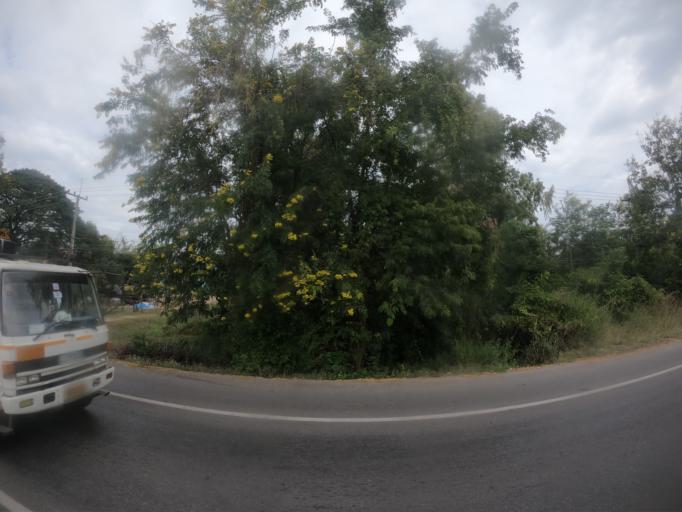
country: TH
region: Maha Sarakham
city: Maha Sarakham
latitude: 16.1444
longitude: 103.4168
